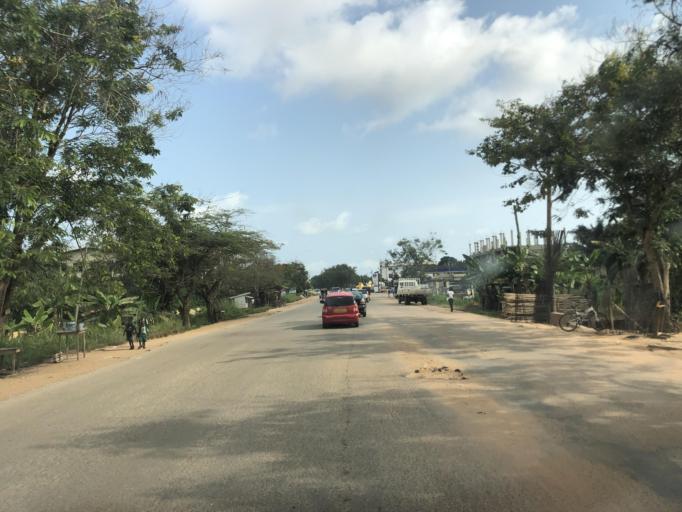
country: GH
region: Central
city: Cape Coast
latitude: 5.1396
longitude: -1.2815
